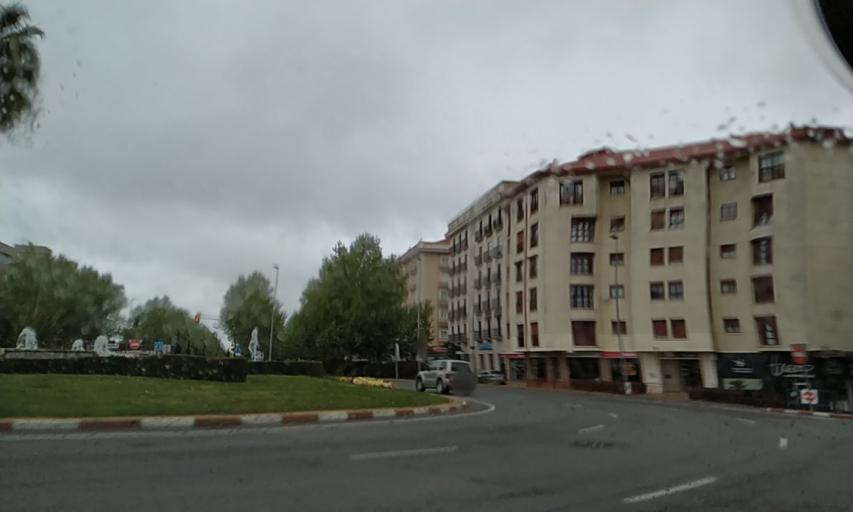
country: ES
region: Extremadura
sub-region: Provincia de Caceres
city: Caceres
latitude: 39.4713
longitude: -6.3881
